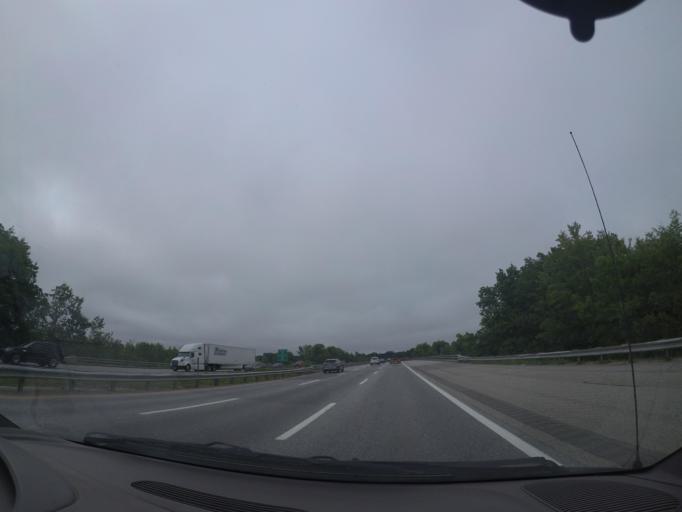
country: US
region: Maine
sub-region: York County
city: Biddeford
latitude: 43.4991
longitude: -70.4895
